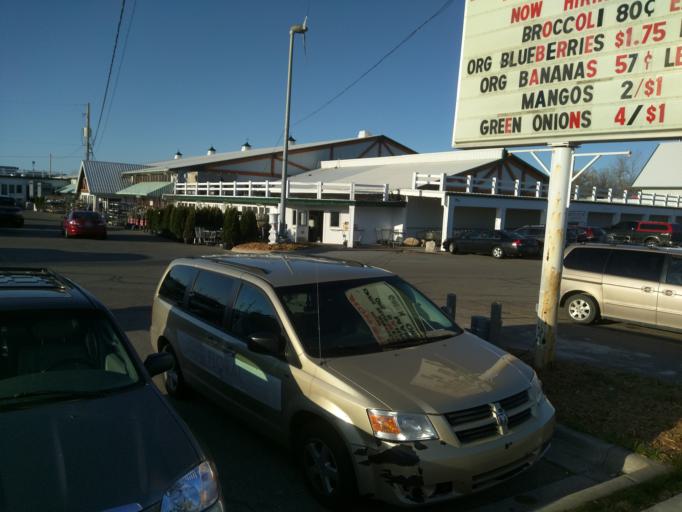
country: US
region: Michigan
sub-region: Eaton County
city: Waverly
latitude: 42.7412
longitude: -84.6614
